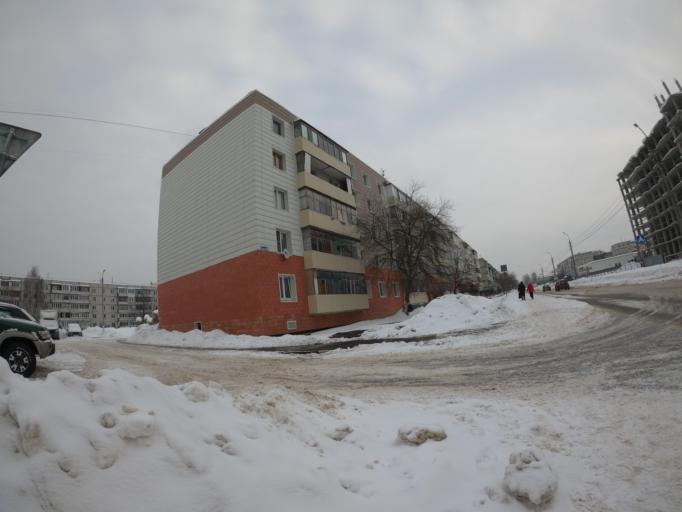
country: RU
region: Moskovskaya
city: Elektrogorsk
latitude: 55.8839
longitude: 38.7763
